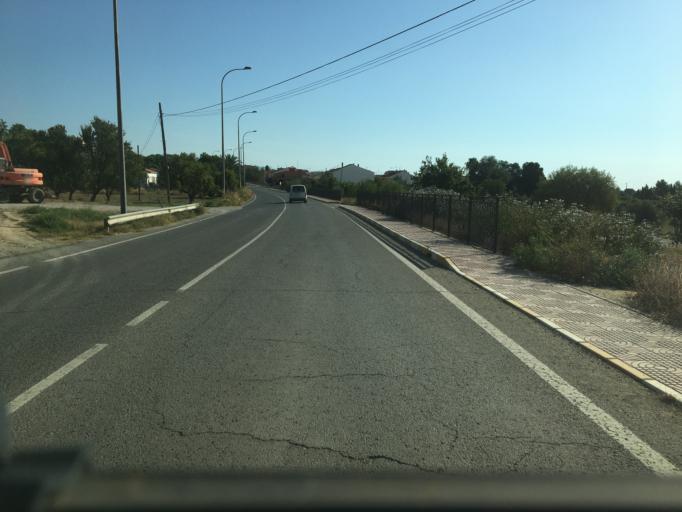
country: ES
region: Murcia
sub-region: Murcia
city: Puerto Lumbreras
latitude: 37.5543
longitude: -1.8112
